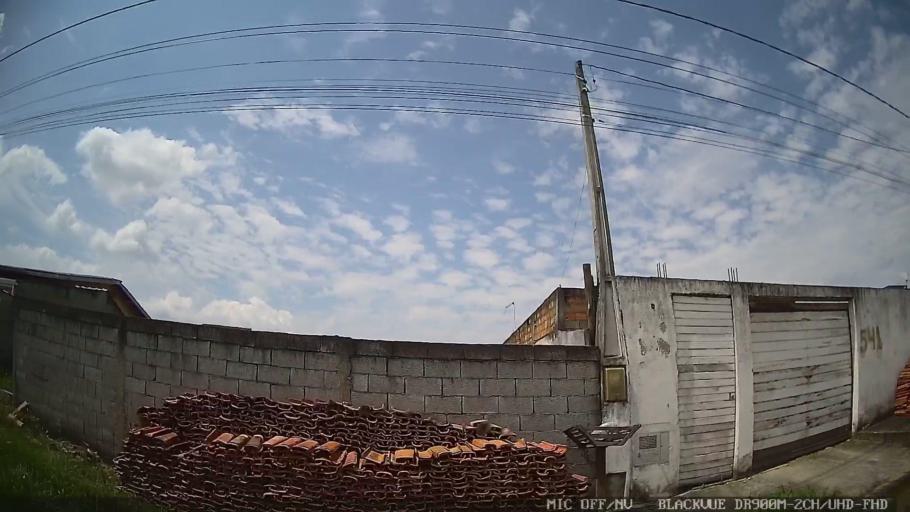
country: BR
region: Sao Paulo
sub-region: Caraguatatuba
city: Caraguatatuba
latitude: -23.6719
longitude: -45.4538
